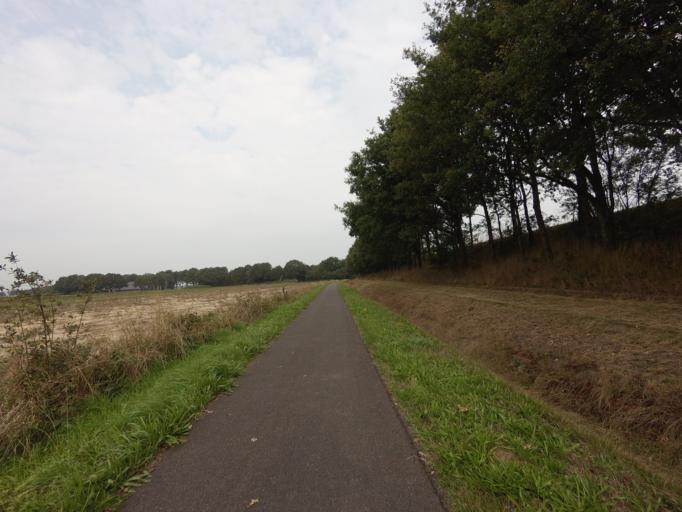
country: NL
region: Drenthe
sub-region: Gemeente Westerveld
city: Dwingeloo
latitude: 52.8859
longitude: 6.4590
